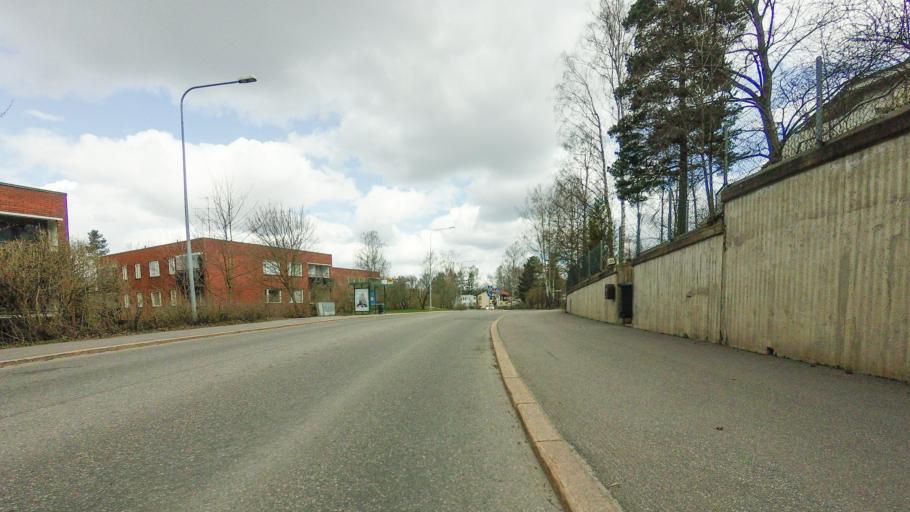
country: FI
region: Uusimaa
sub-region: Helsinki
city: Vantaa
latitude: 60.2225
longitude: 25.0933
